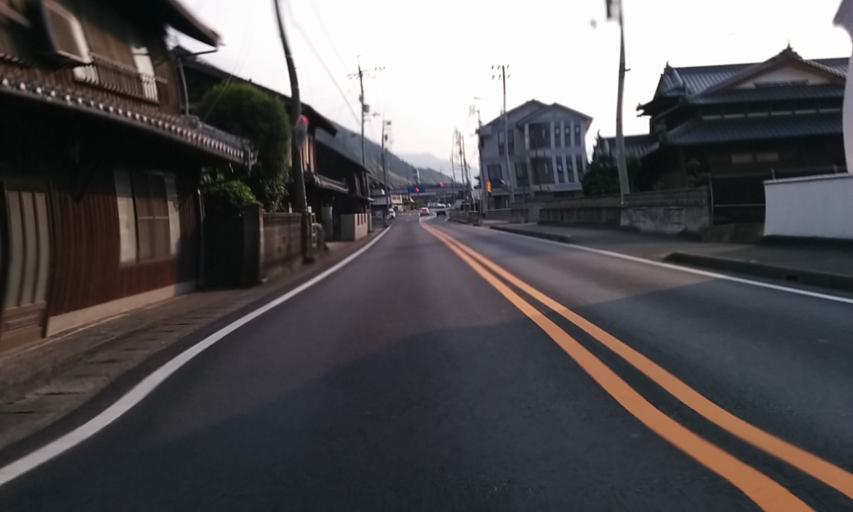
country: JP
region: Ehime
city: Saijo
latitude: 33.8830
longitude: 133.0791
